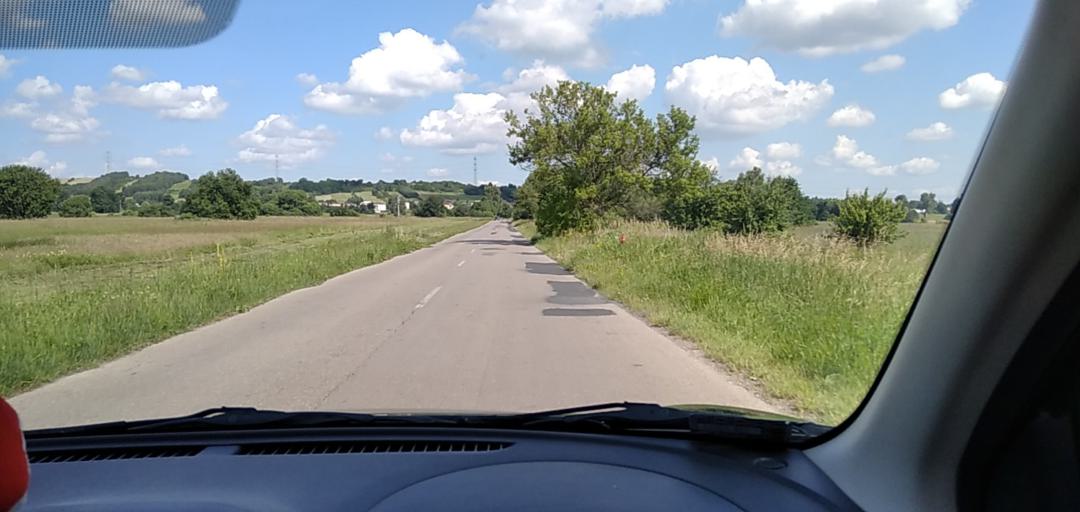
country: PL
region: Silesian Voivodeship
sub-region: Powiat bedzinski
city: Sarnow
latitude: 50.3952
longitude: 19.1393
